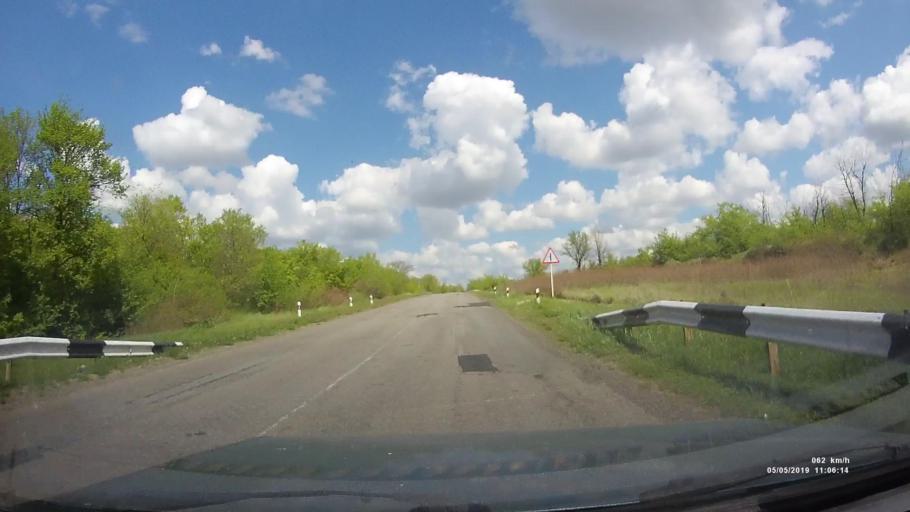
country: RU
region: Rostov
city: Ust'-Donetskiy
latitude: 47.7135
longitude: 40.9110
